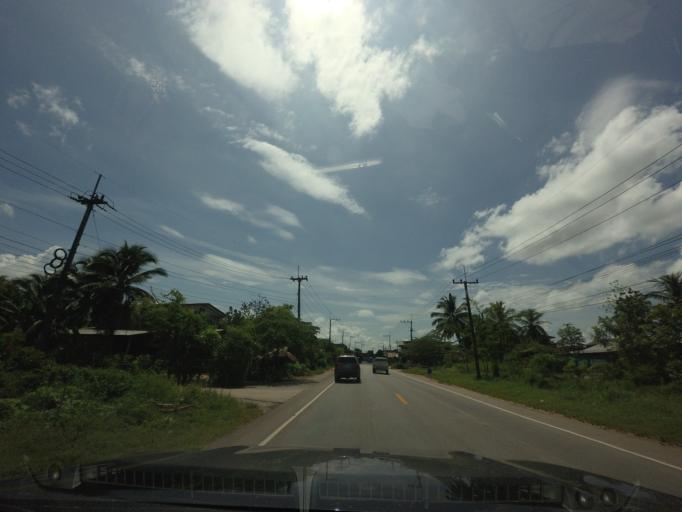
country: TH
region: Changwat Udon Thani
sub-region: Amphoe Ban Phue
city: Ban Phue
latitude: 17.7507
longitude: 102.3989
